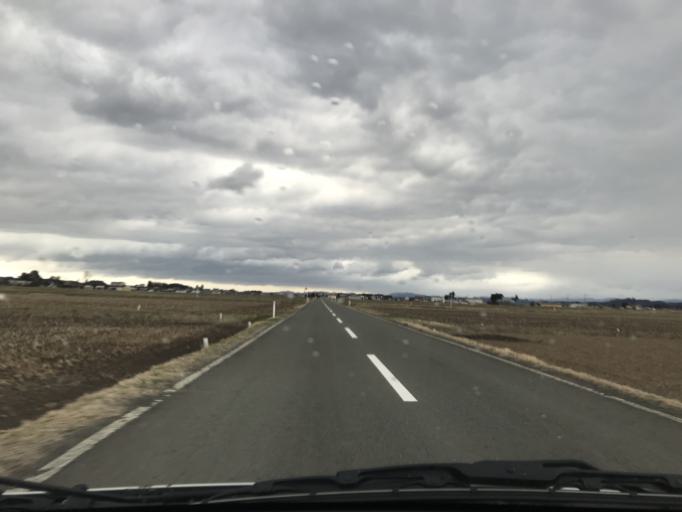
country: JP
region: Iwate
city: Mizusawa
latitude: 39.0946
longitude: 141.1628
